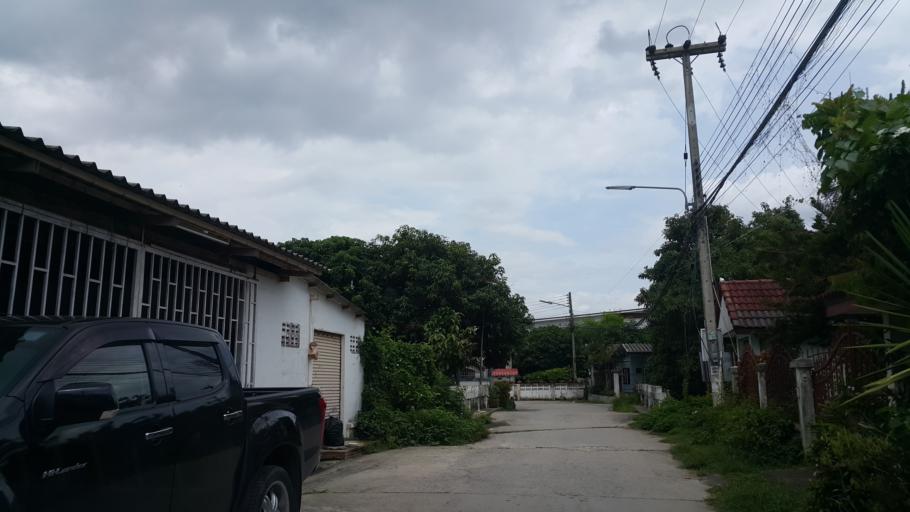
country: TH
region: Chiang Mai
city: San Sai
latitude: 18.8185
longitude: 99.0254
